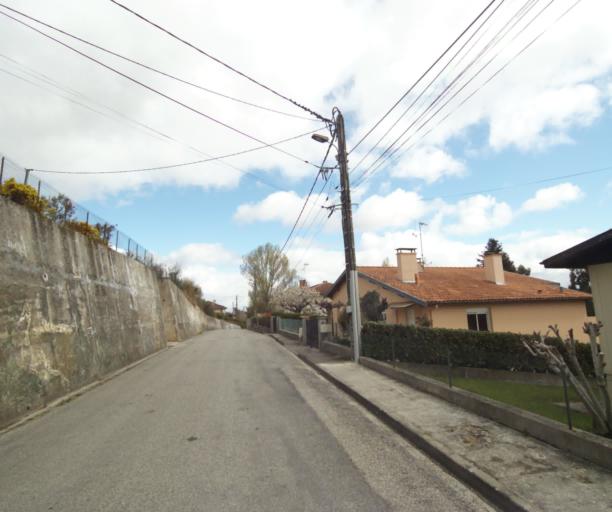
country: FR
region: Midi-Pyrenees
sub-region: Departement de l'Ariege
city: Saverdun
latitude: 43.2296
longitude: 1.5704
